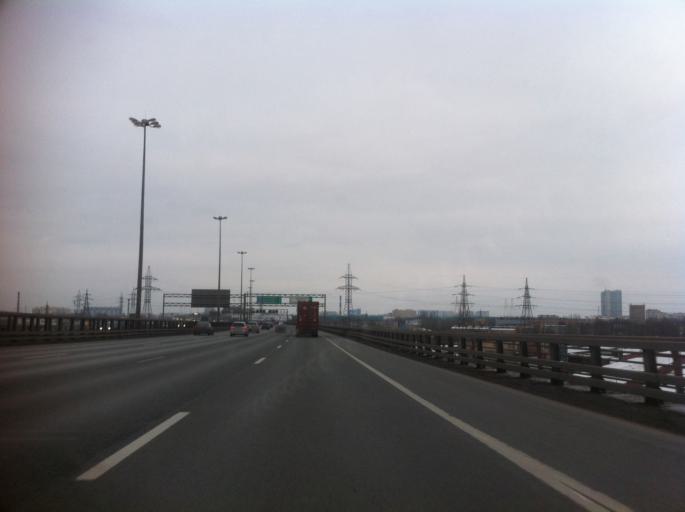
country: RU
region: St.-Petersburg
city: Obukhovo
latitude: 59.8354
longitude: 30.4493
